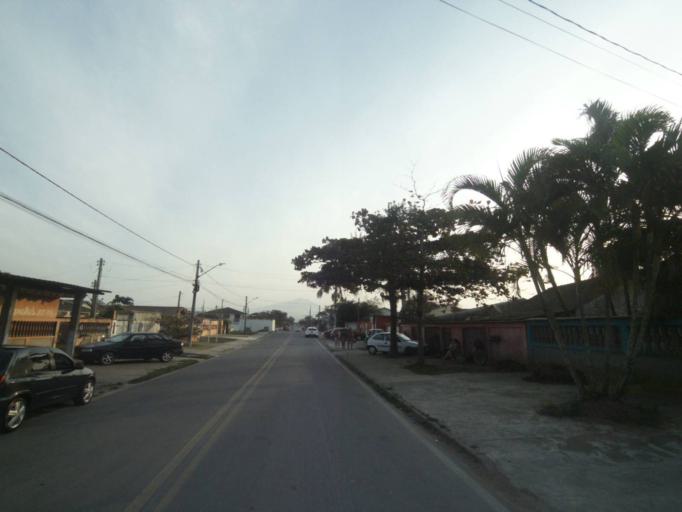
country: BR
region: Parana
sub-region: Paranagua
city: Paranagua
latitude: -25.5135
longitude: -48.5390
